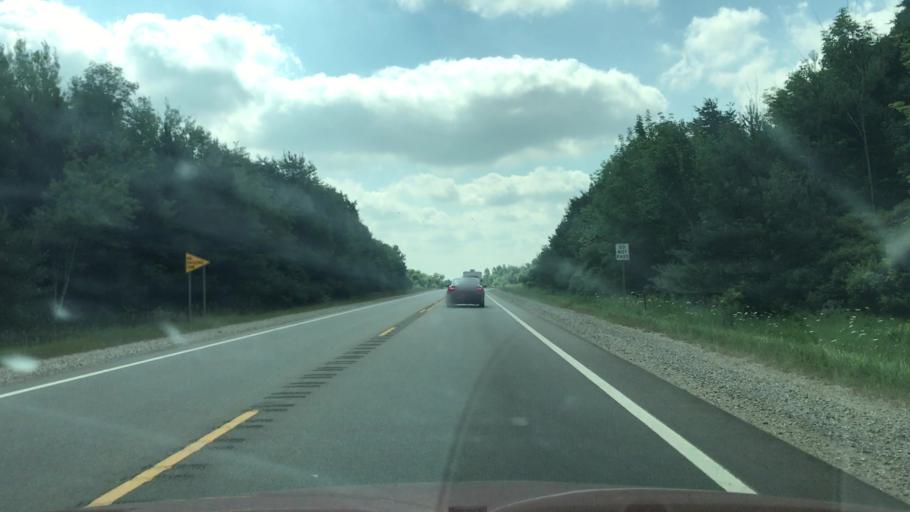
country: US
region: Michigan
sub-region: Kent County
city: Kent City
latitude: 43.2083
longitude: -85.7440
